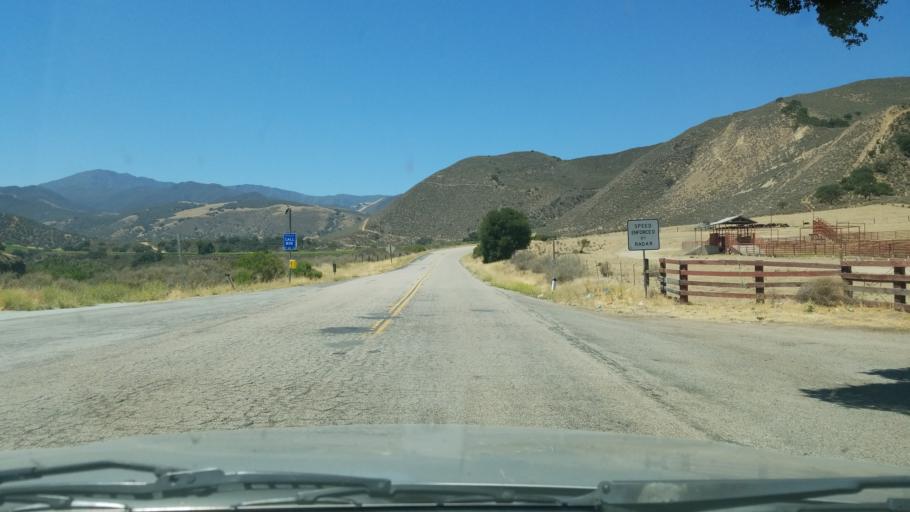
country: US
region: California
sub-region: Monterey County
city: Greenfield
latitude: 36.2801
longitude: -121.3266
